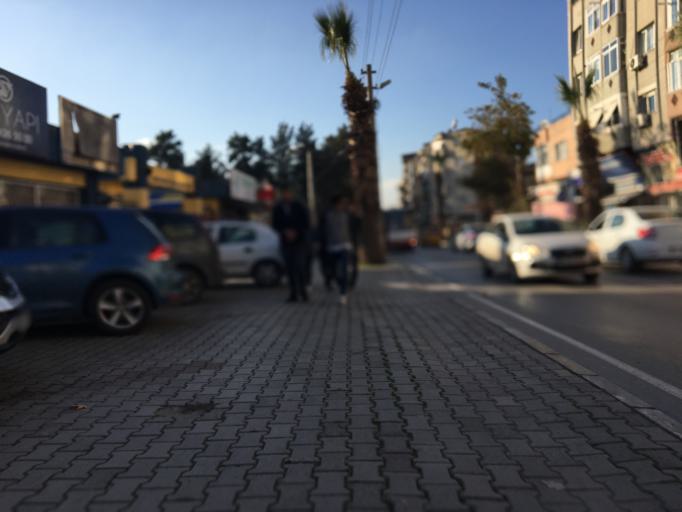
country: TR
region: Izmir
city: Buca
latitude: 38.3828
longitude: 27.1732
